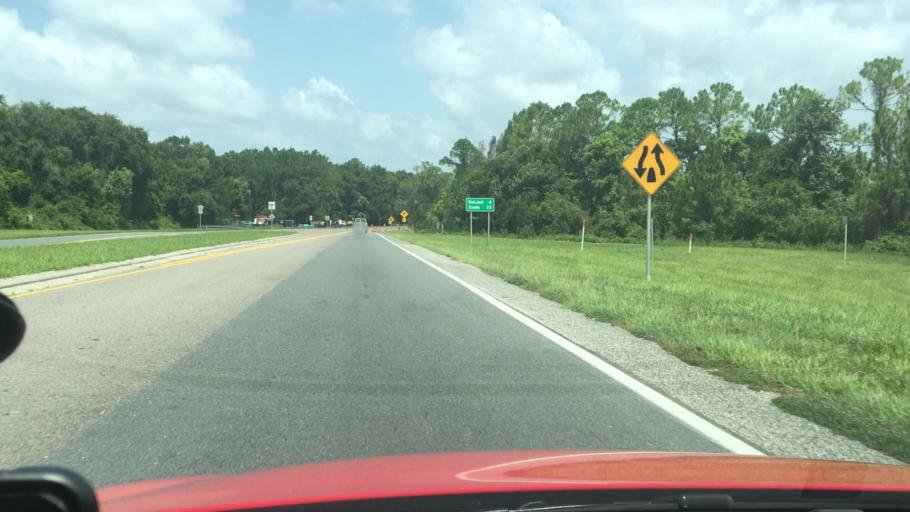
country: US
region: Florida
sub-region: Volusia County
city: Lake Helen
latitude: 29.0160
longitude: -81.2479
